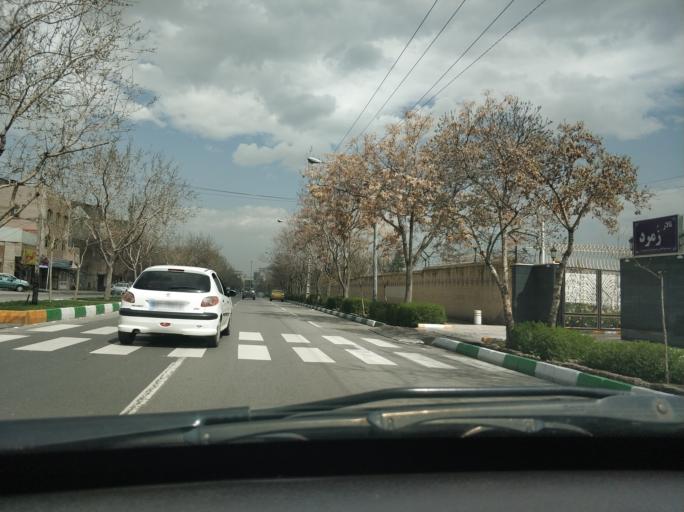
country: IR
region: Razavi Khorasan
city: Mashhad
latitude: 36.2812
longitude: 59.5775
